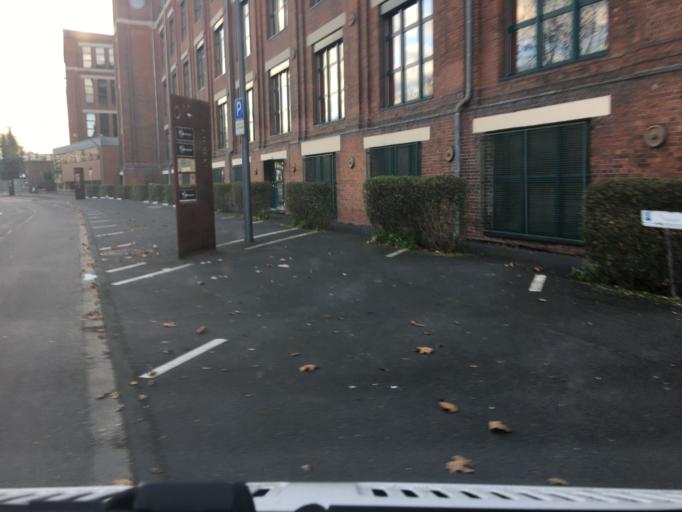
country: DE
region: North Rhine-Westphalia
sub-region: Regierungsbezirk Koln
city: Muelheim
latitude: 50.9715
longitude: 7.0177
